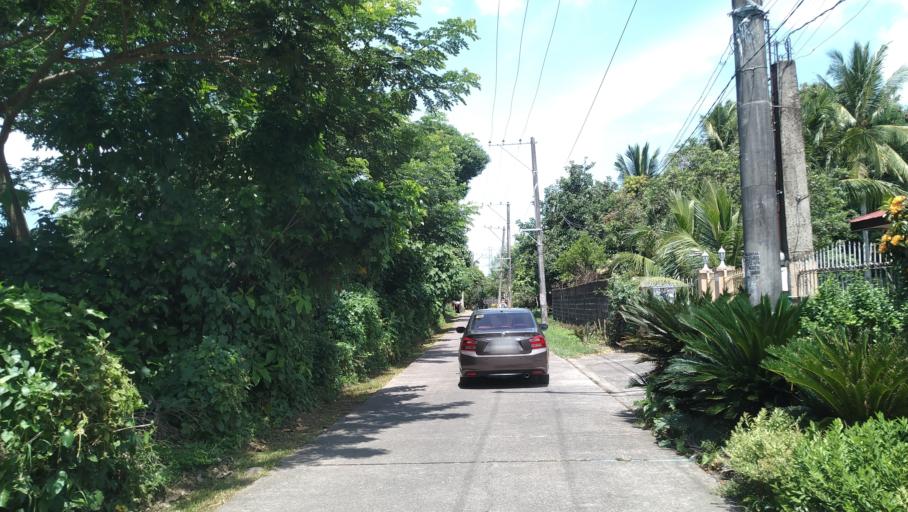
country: PH
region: Calabarzon
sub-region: Province of Laguna
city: Cabanbanan
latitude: 14.2508
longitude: 121.4156
